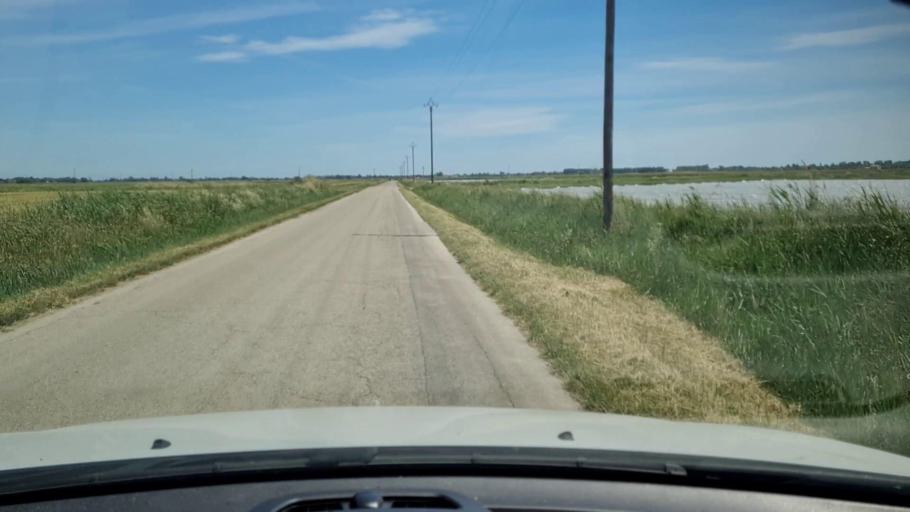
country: FR
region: Languedoc-Roussillon
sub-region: Departement du Gard
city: Saint-Gilles
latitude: 43.6066
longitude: 4.4327
